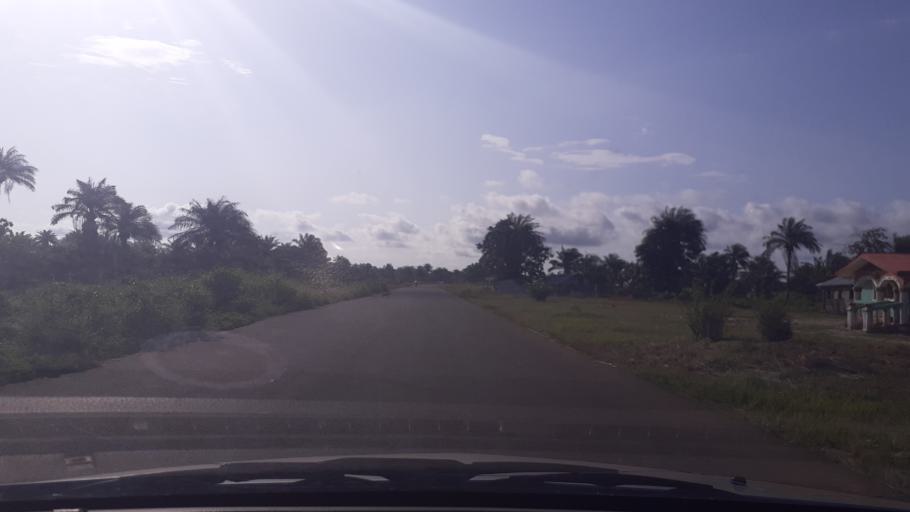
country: LR
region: Montserrado
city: Bensonville City
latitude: 6.1689
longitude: -10.4469
